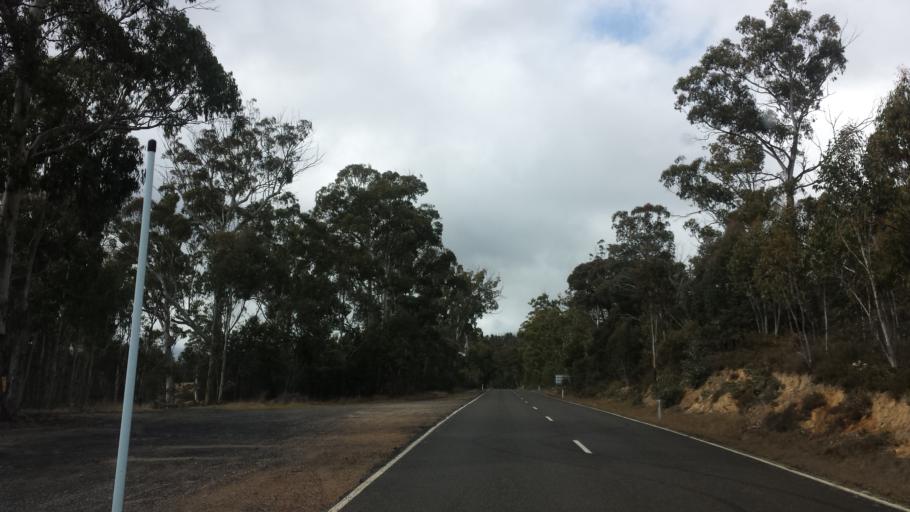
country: AU
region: Victoria
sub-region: Alpine
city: Mount Beauty
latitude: -37.1315
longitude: 147.5203
